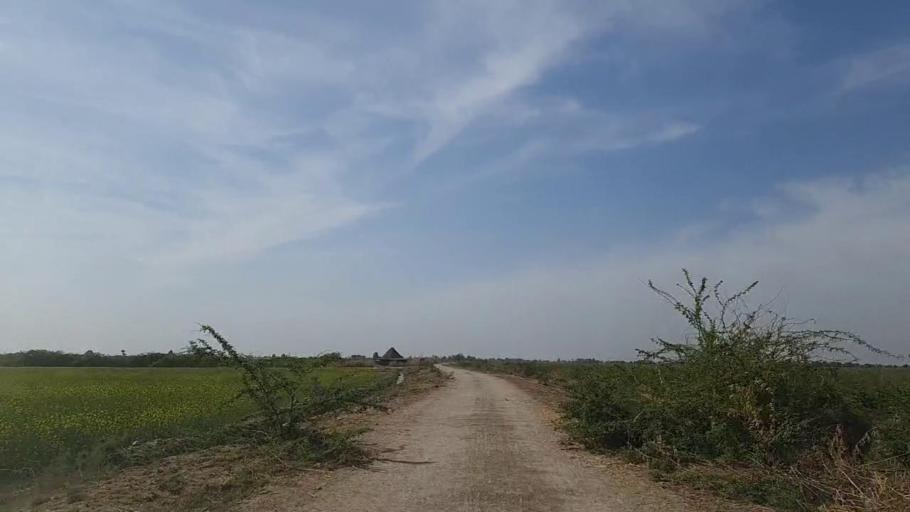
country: PK
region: Sindh
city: Samaro
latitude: 25.2068
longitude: 69.4460
